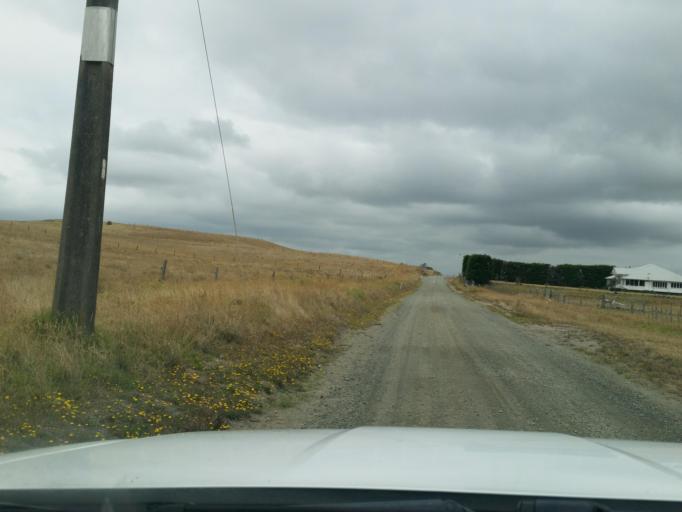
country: NZ
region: Northland
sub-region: Kaipara District
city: Dargaville
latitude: -35.9893
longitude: 173.8264
